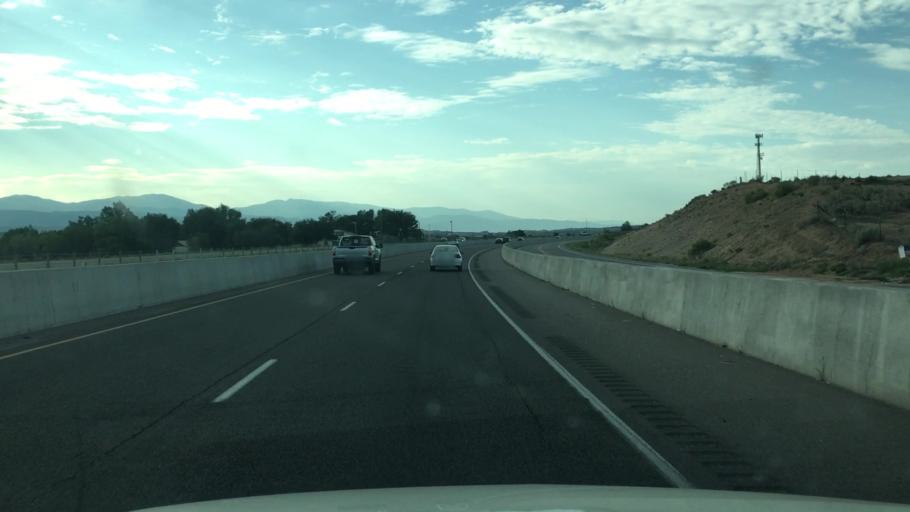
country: US
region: New Mexico
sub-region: Santa Fe County
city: El Valle de Arroyo Seco
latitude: 35.9586
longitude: -106.0245
